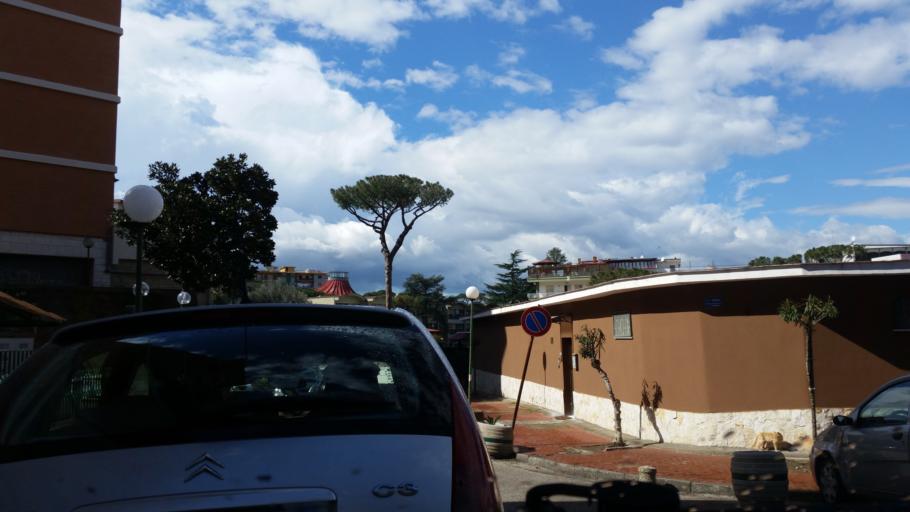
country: IT
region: Campania
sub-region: Provincia di Napoli
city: Napoli
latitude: 40.8725
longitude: 14.2400
